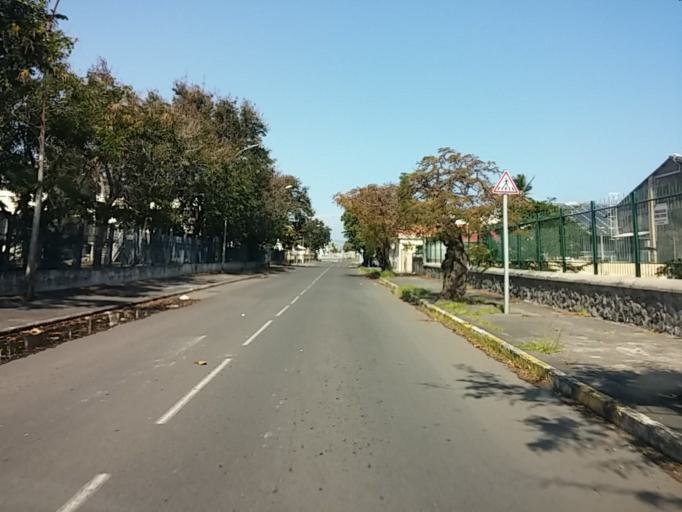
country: RE
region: Reunion
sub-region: Reunion
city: Le Port
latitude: -20.9333
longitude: 55.2900
